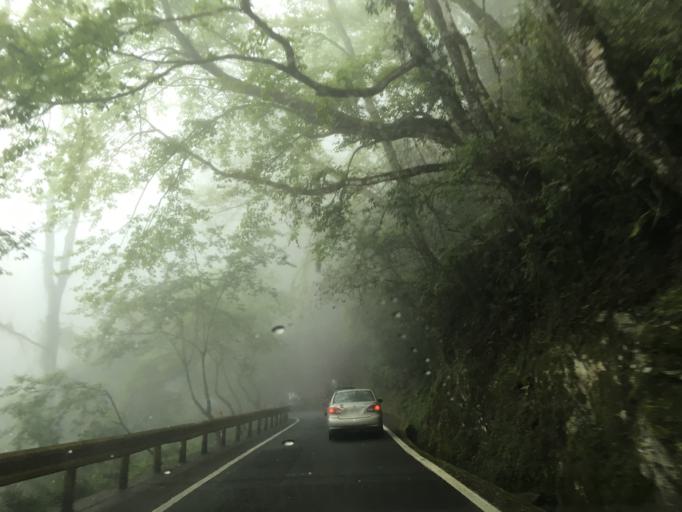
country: TW
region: Taiwan
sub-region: Hualien
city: Hualian
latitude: 24.1856
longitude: 121.4168
